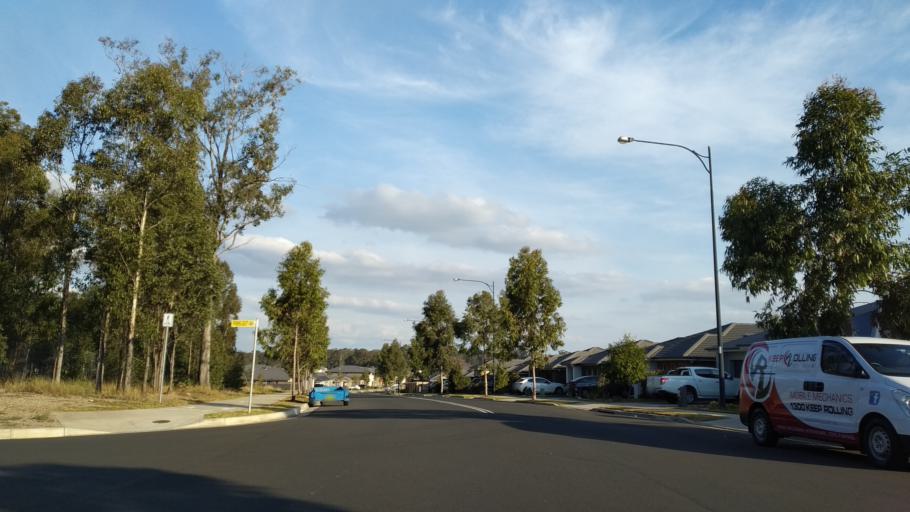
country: AU
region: New South Wales
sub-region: Penrith Municipality
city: Werrington Downs
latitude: -33.7233
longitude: 150.7356
